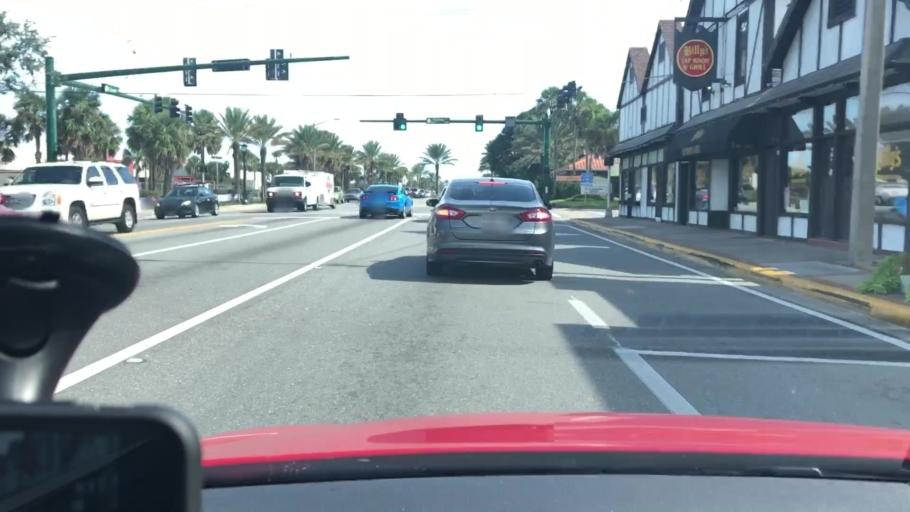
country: US
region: Florida
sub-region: Volusia County
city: Ormond Beach
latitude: 29.2896
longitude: -81.0458
